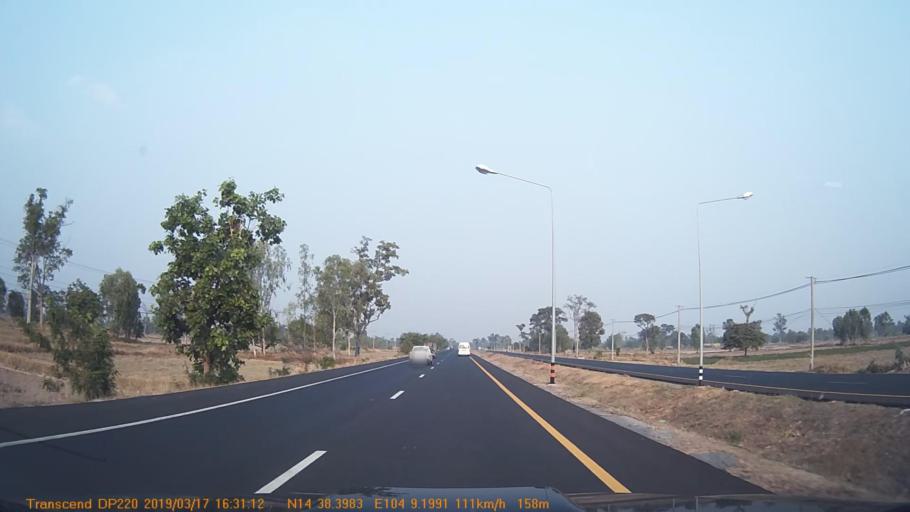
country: TH
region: Sisaket
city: Khu Khan
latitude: 14.6400
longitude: 104.1538
